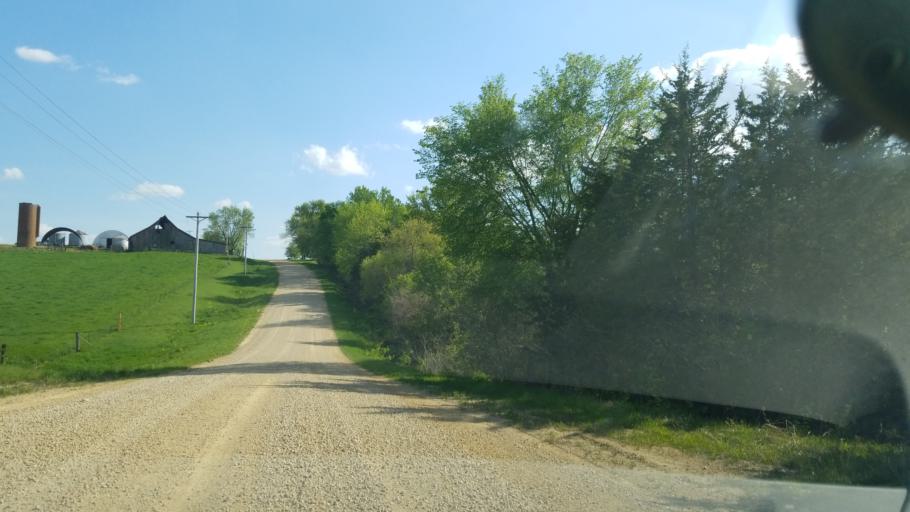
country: US
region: Iowa
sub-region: Jackson County
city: Maquoketa
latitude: 42.2091
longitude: -90.7296
